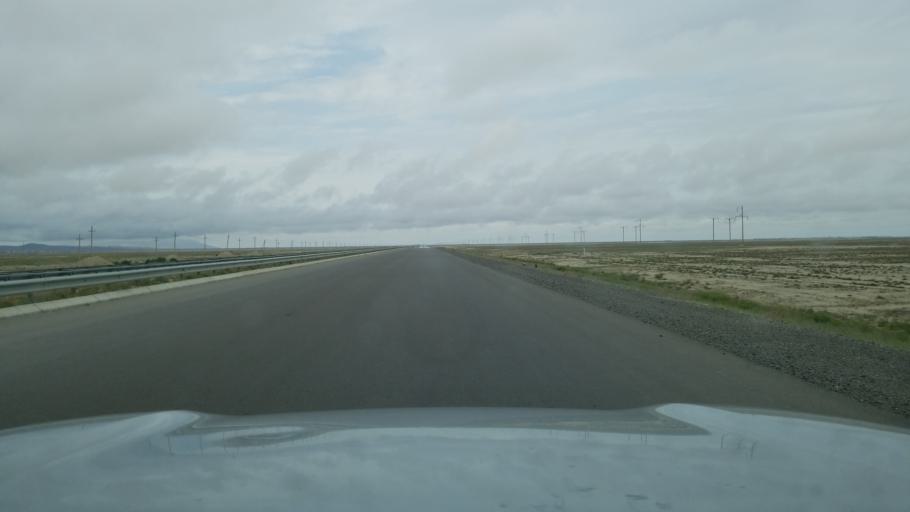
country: TM
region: Balkan
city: Serdar
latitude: 39.1124
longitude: 55.9212
